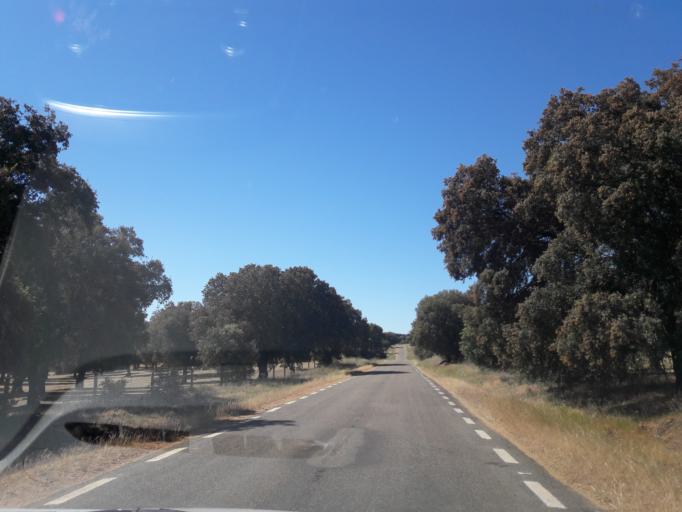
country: ES
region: Castille and Leon
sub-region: Provincia de Salamanca
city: Parada de Arriba
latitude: 41.0136
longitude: -5.8148
